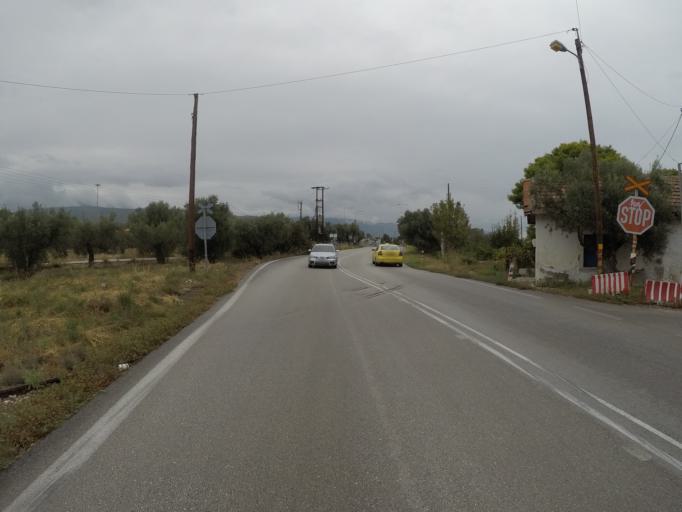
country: GR
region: Peloponnese
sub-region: Nomos Korinthias
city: Agioi Theodoroi
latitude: 37.9198
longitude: 23.1199
